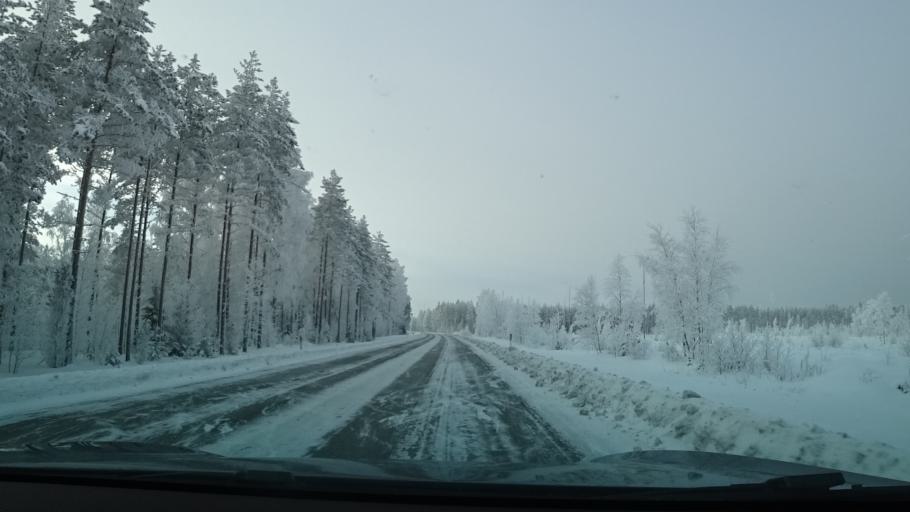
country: FI
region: South Karelia
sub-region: Imatra
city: Saari
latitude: 61.7790
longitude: 29.7010
